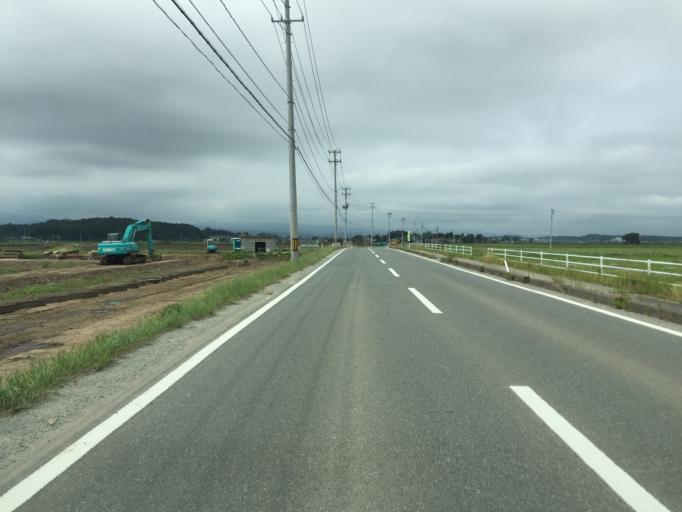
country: JP
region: Fukushima
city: Namie
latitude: 37.6853
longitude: 140.9915
